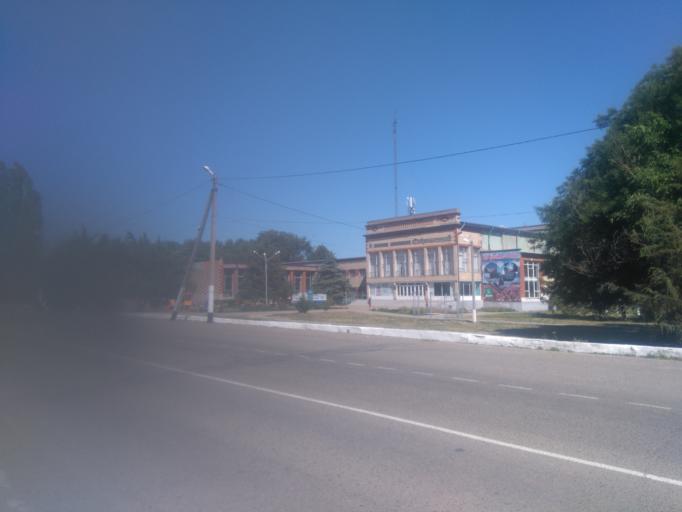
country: RU
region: Krasnodarskiy
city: Fastovetskaya
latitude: 45.9170
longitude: 40.1530
